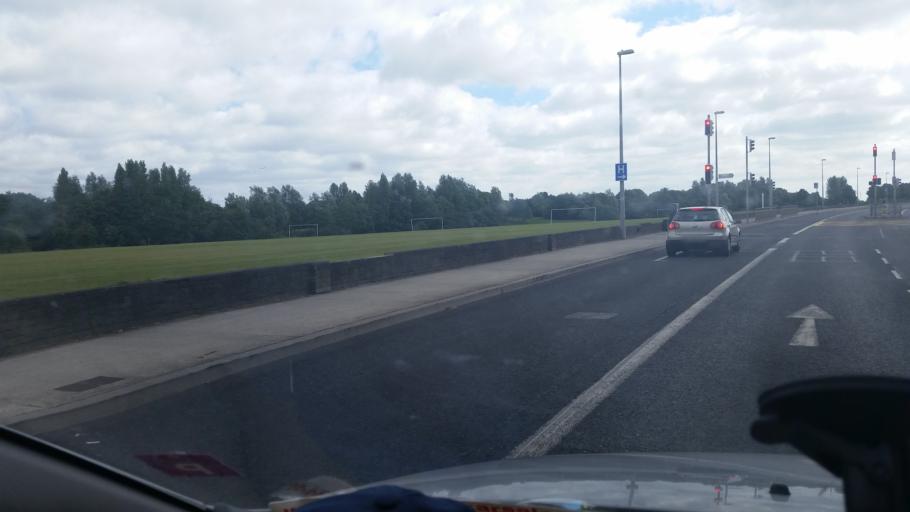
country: IE
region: Leinster
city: Artane
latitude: 53.3979
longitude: -6.2248
